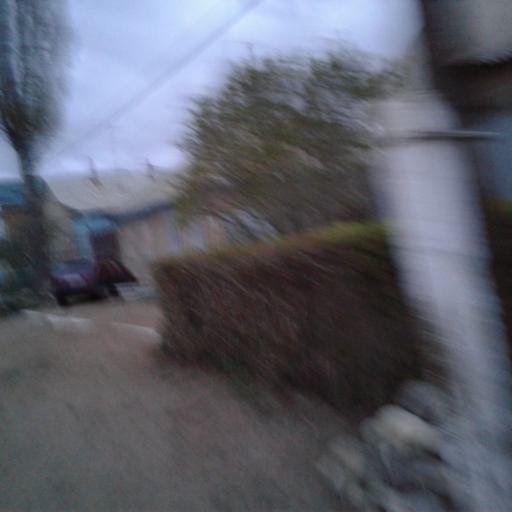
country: KG
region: Ysyk-Koel
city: Bokombayevskoye
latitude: 42.1088
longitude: 76.9859
